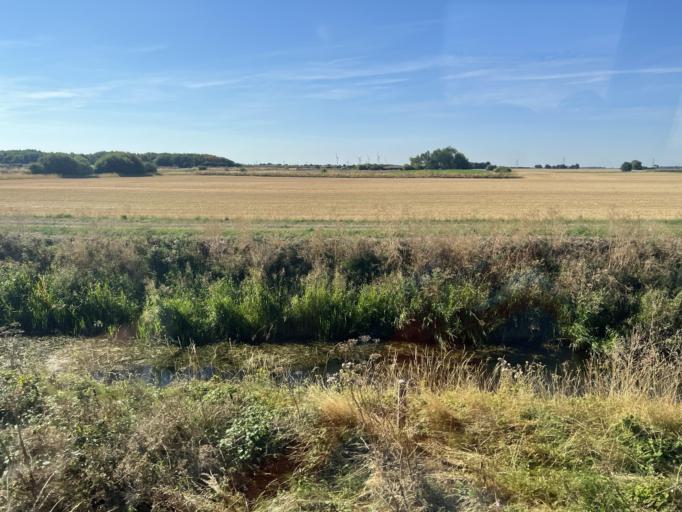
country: GB
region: England
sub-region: Lincolnshire
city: Donington
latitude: 52.9665
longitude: -0.2209
